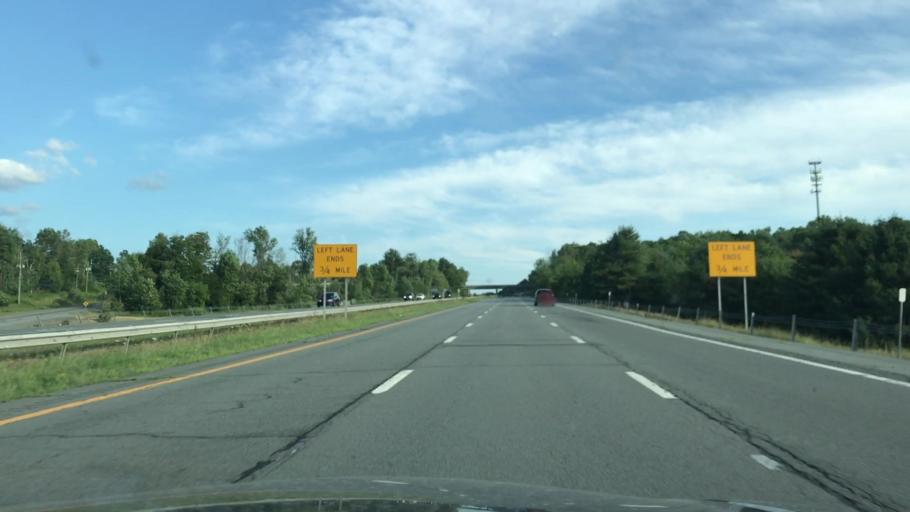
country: US
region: New York
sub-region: Sullivan County
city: Monticello
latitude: 41.7009
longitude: -74.7354
